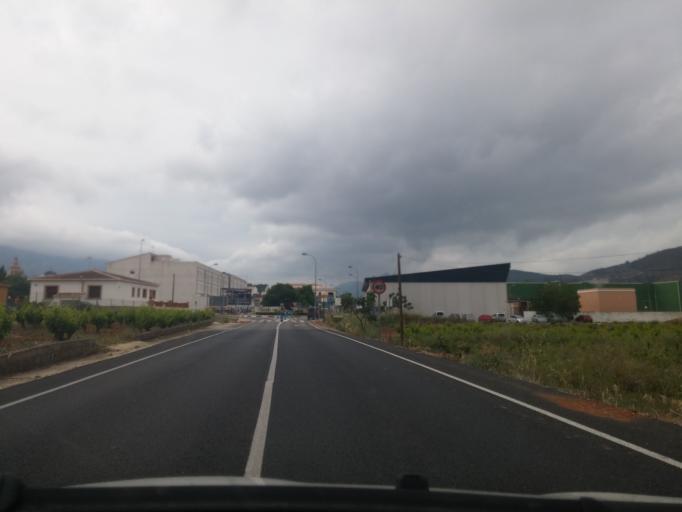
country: ES
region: Valencia
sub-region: Provincia de Alicante
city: Jalon
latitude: 38.7419
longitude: -0.0065
